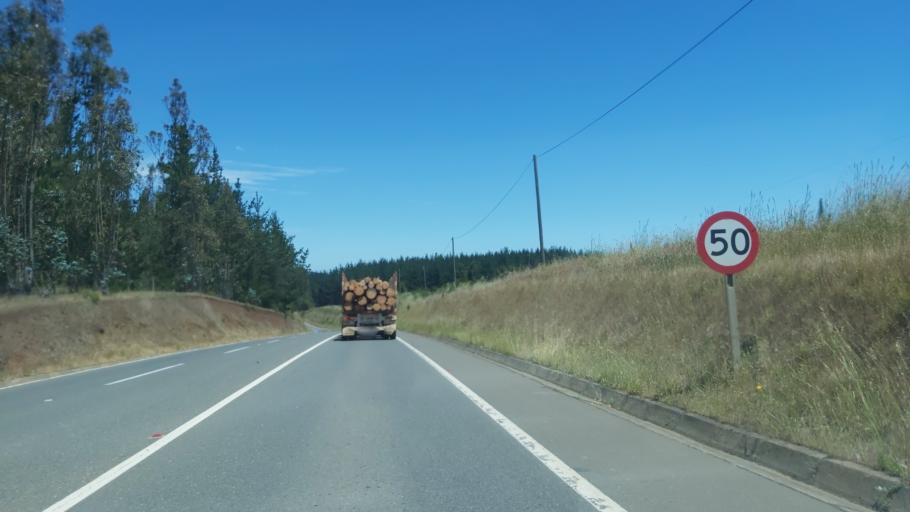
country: CL
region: Maule
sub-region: Provincia de Talca
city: Constitucion
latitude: -35.1503
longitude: -72.2138
